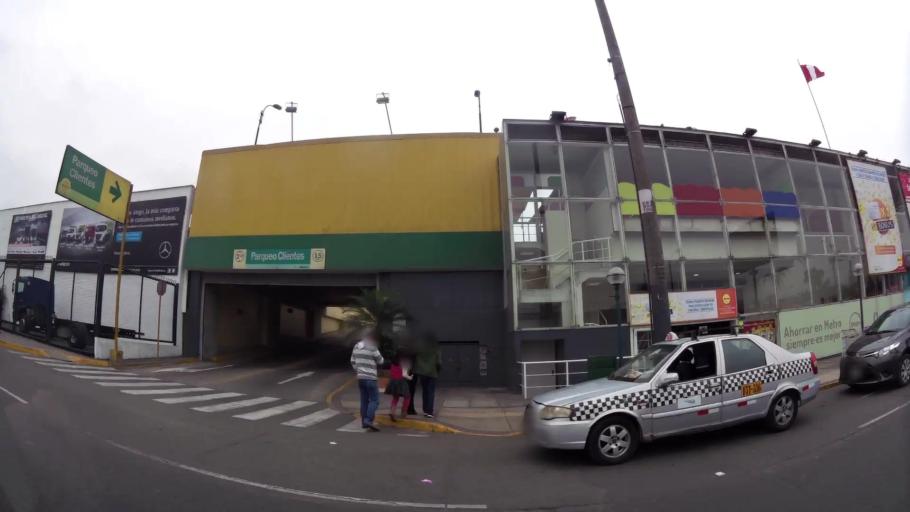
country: PE
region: Lima
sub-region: Lima
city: San Luis
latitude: -12.0838
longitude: -77.0133
